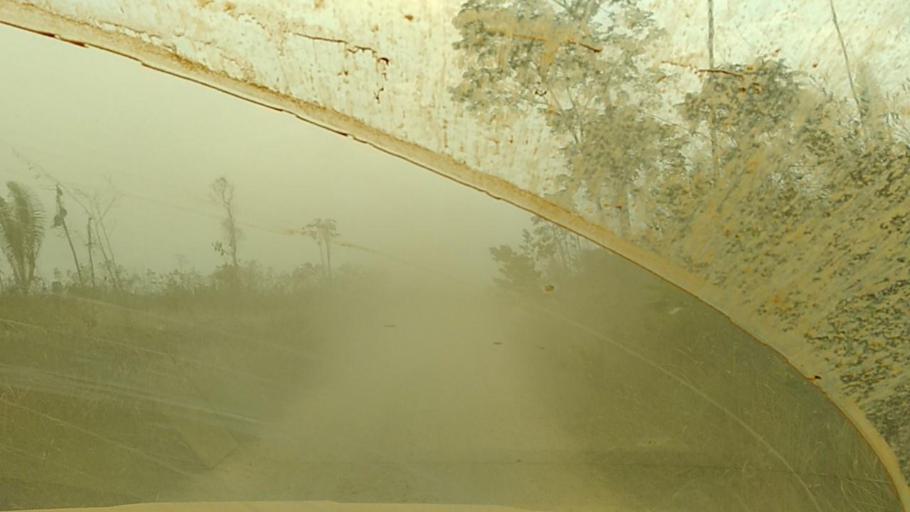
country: BR
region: Rondonia
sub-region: Porto Velho
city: Porto Velho
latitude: -8.7732
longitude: -63.2077
